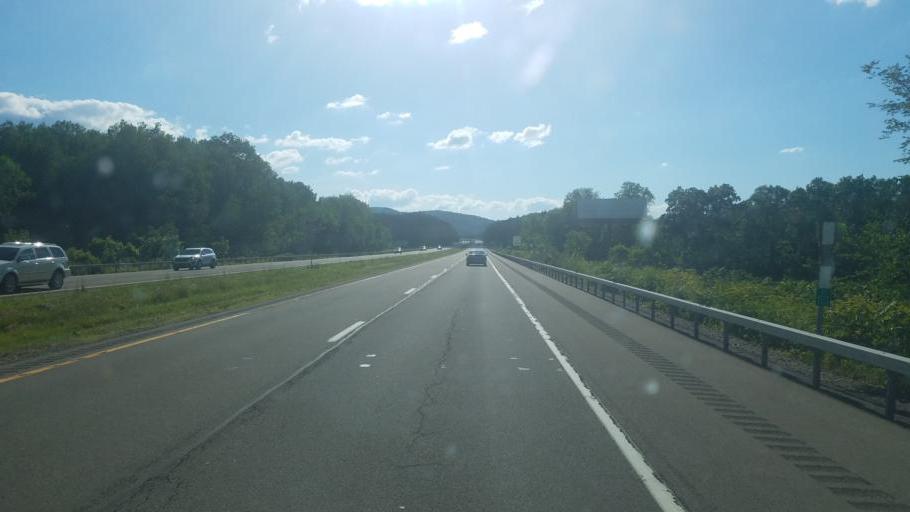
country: US
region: New York
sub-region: Cattaraugus County
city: Randolph
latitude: 42.1047
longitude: -78.8803
